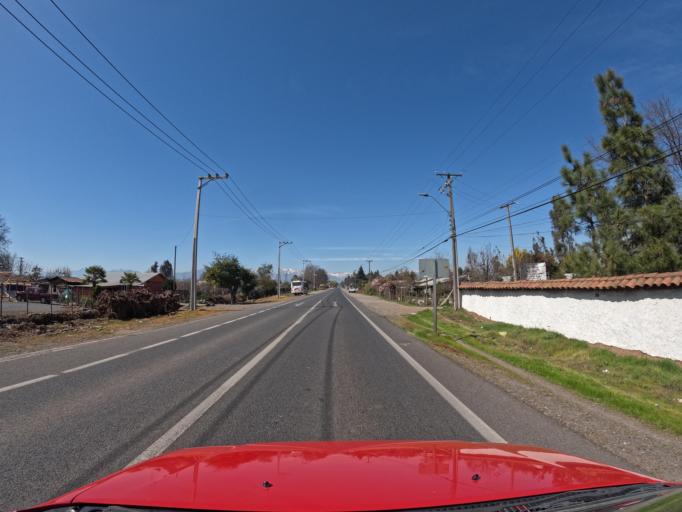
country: CL
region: Maule
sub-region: Provincia de Curico
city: Teno
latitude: -34.9615
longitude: -71.0922
